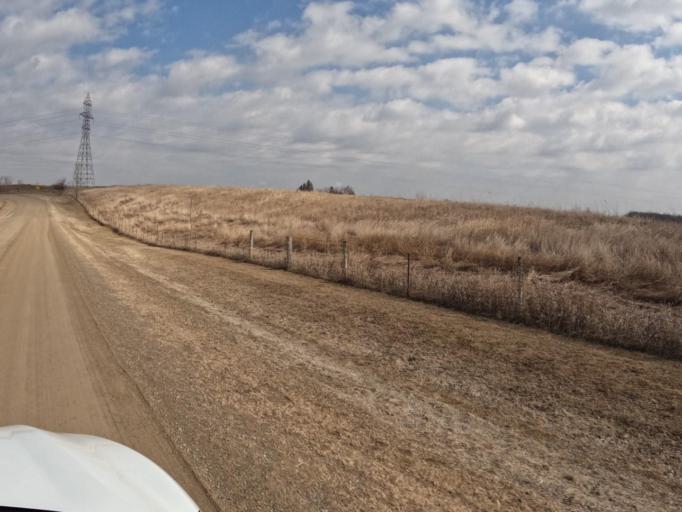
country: CA
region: Ontario
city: Shelburne
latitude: 43.9404
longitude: -80.2437
